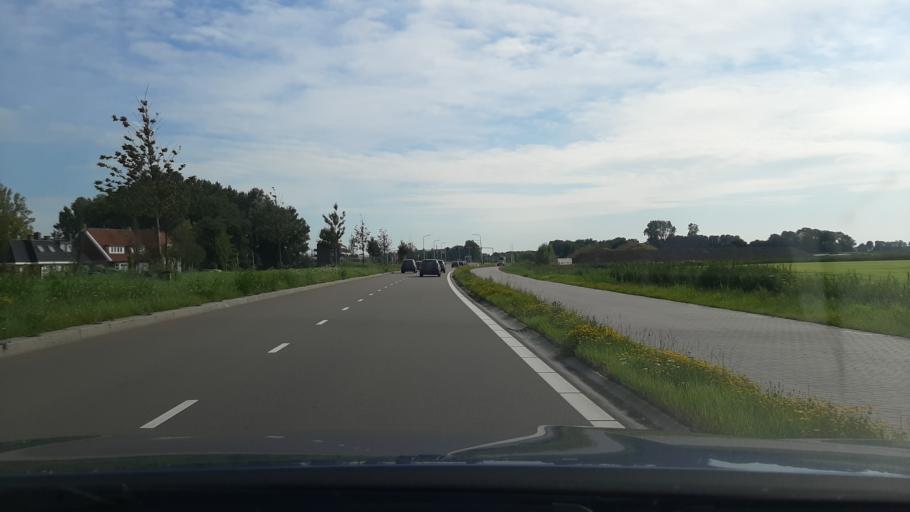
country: NL
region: Friesland
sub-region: Gemeente Leeuwarden
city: Goutum
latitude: 53.1755
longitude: 5.7941
